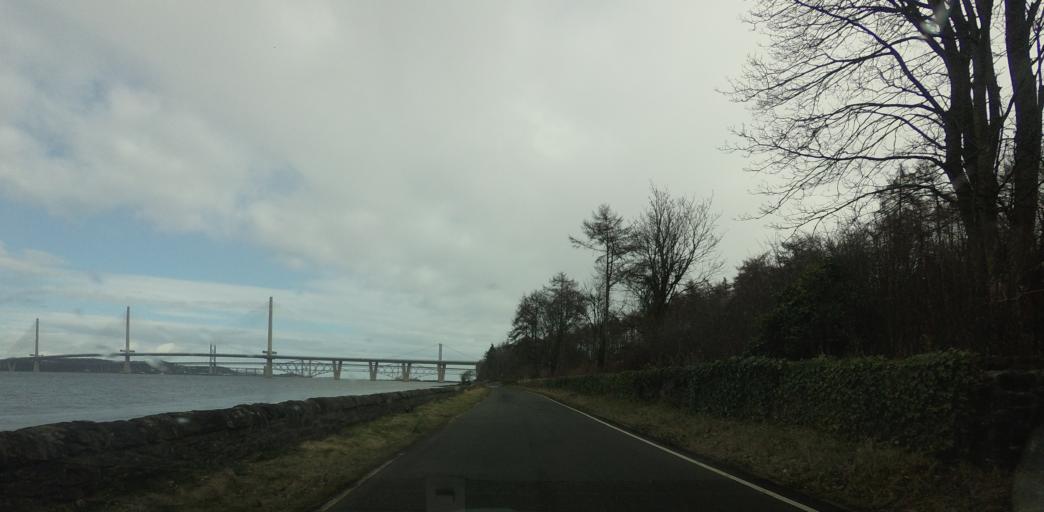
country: GB
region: Scotland
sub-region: Edinburgh
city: Queensferry
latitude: 55.9932
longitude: -3.4328
